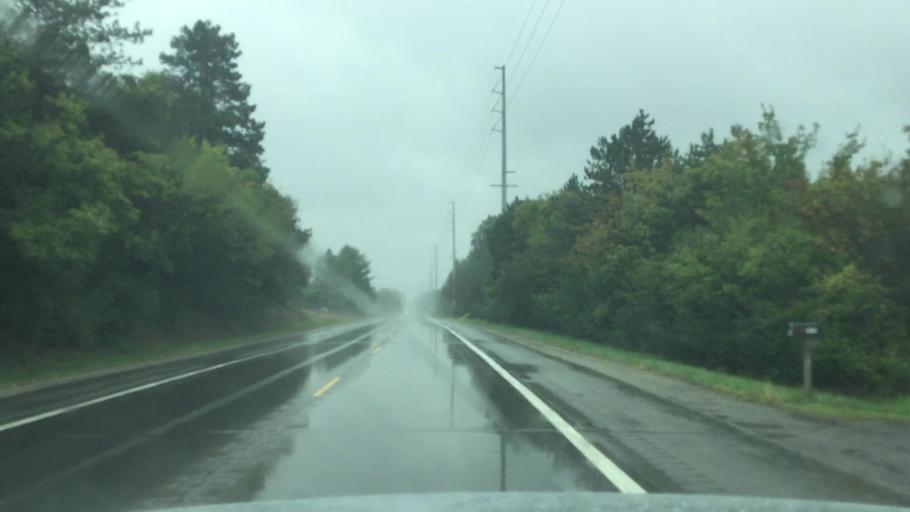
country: US
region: Michigan
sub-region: Livingston County
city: Brighton
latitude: 42.6310
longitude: -83.8052
